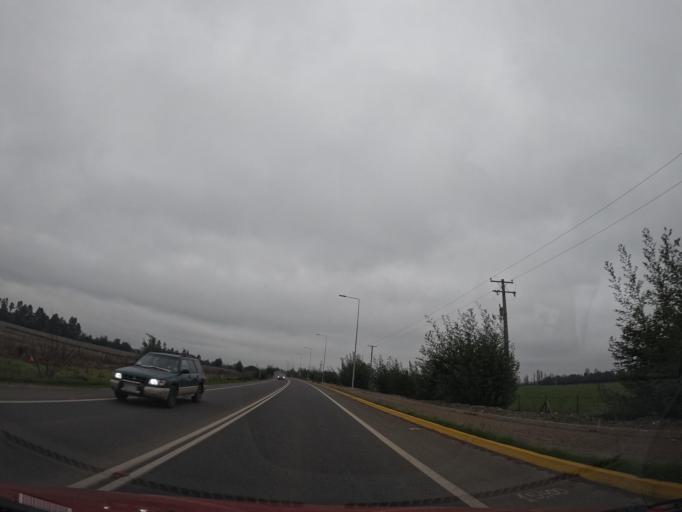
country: CL
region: Maule
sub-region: Provincia de Talca
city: San Clemente
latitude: -35.5129
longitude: -71.5033
